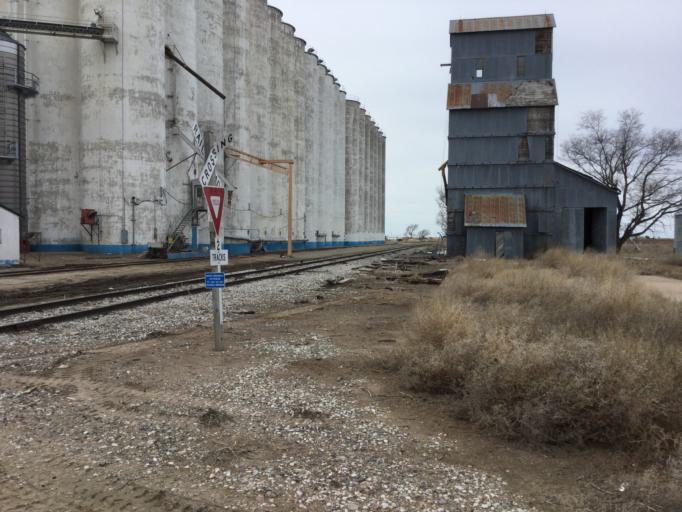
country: US
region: Kansas
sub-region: Lane County
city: Dighton
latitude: 38.4832
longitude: -100.6014
